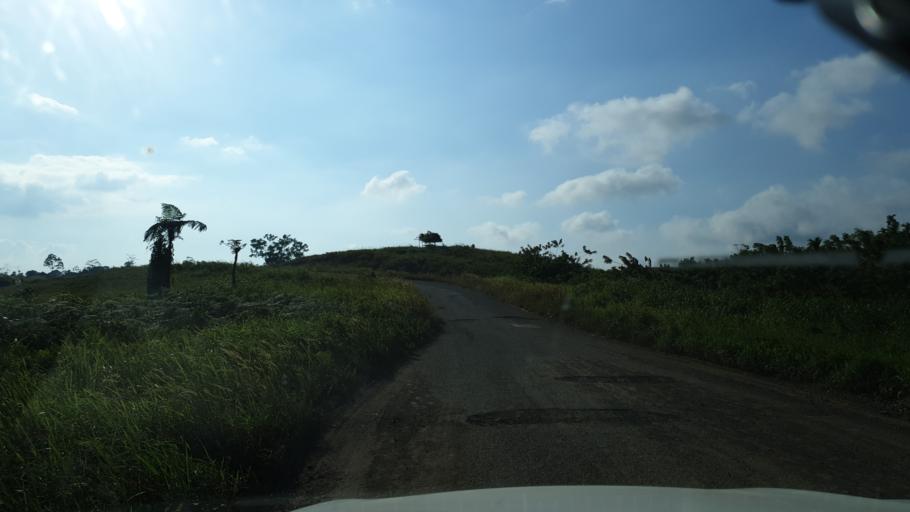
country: PG
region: East Sepik
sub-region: Wewak
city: Wewak
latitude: -3.7018
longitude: 143.7196
